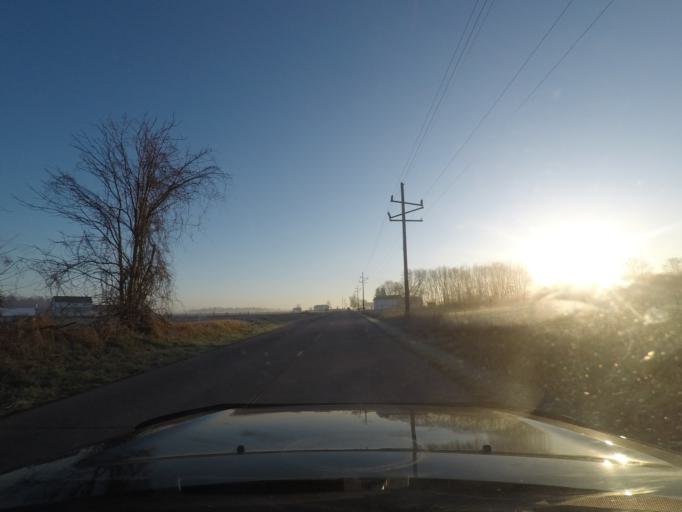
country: US
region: Indiana
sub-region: Marshall County
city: Bremen
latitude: 41.4602
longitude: -86.0820
